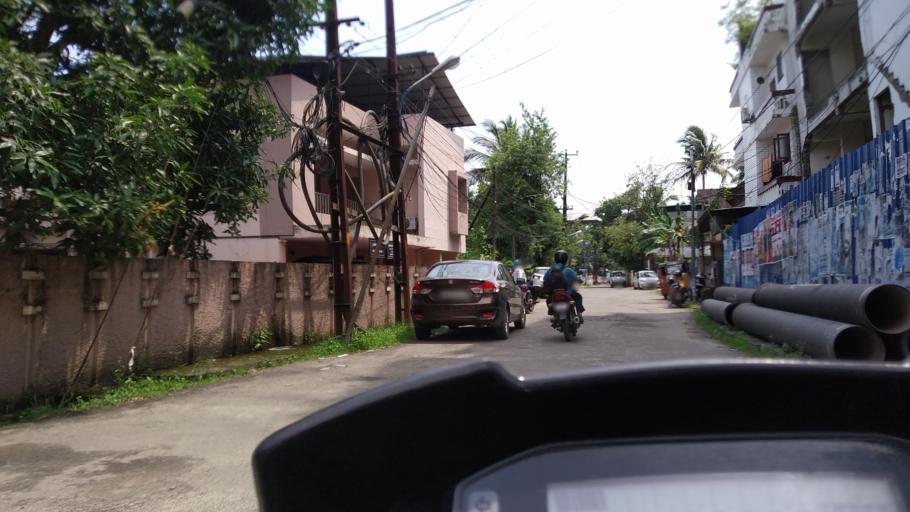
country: IN
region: Kerala
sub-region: Ernakulam
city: Cochin
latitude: 9.9602
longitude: 76.2916
